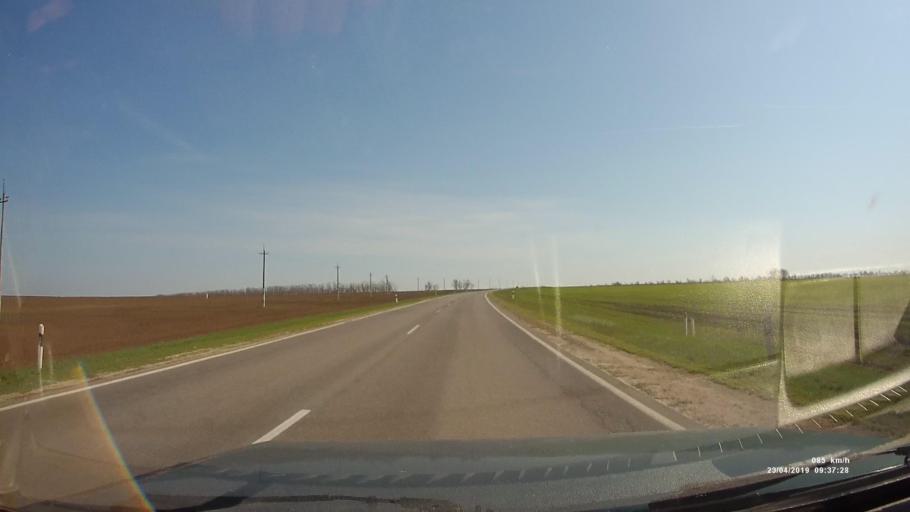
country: RU
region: Rostov
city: Gundorovskiy
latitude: 46.8424
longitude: 41.8925
